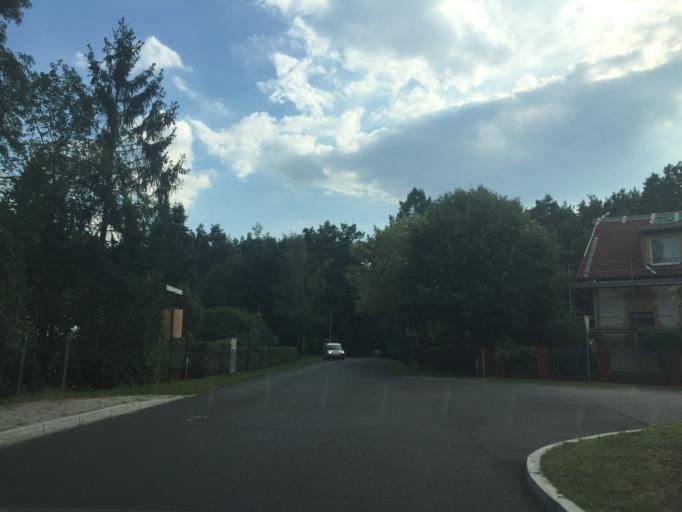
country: DE
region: Brandenburg
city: Erkner
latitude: 52.3814
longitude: 13.7690
